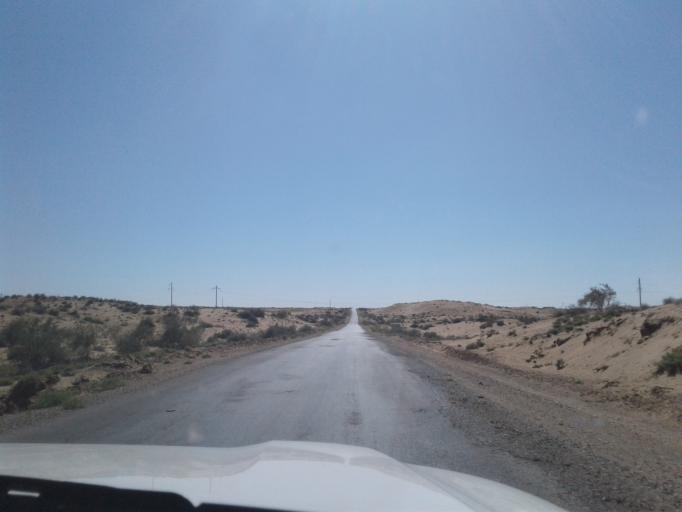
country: AF
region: Badghis
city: Bala Murghab
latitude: 35.9667
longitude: 62.7204
